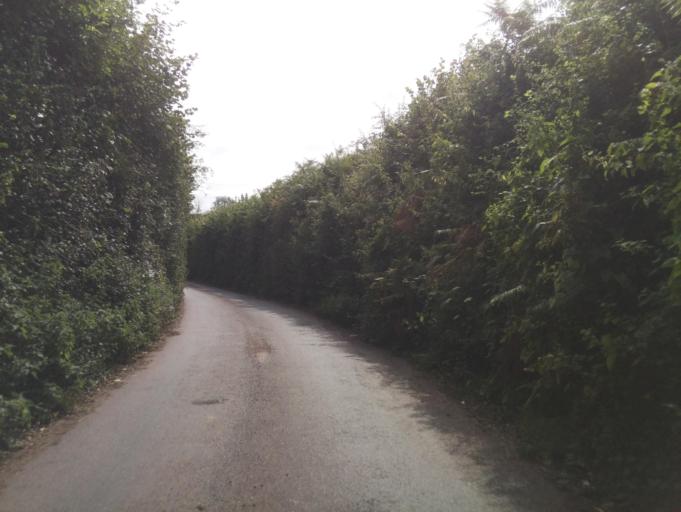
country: GB
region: England
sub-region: Devon
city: Marldon
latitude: 50.4170
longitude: -3.6259
